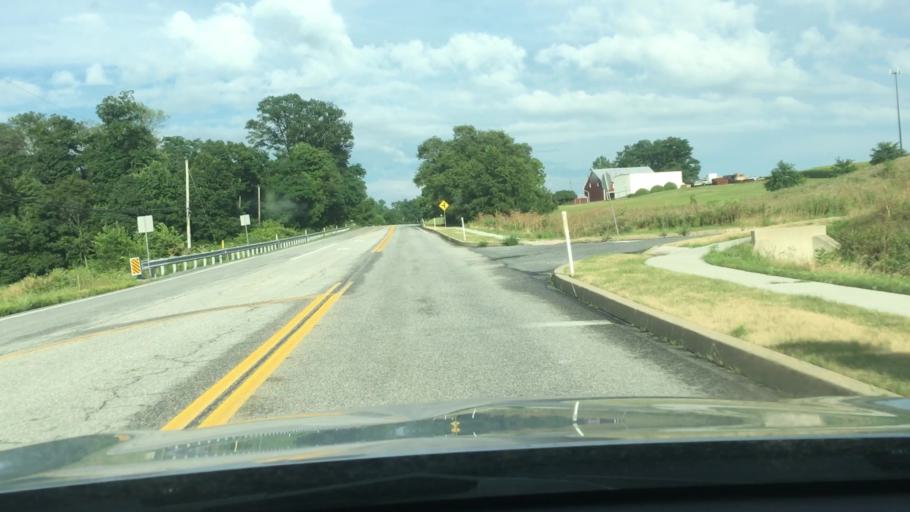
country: US
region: Pennsylvania
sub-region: York County
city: Dillsburg
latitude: 40.1051
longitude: -77.0201
